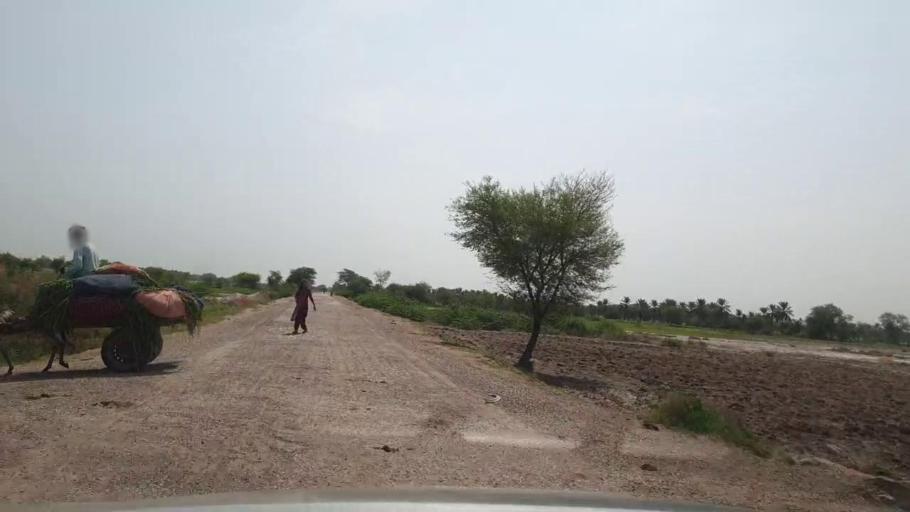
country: PK
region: Sindh
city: Pano Aqil
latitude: 27.6169
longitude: 69.1377
